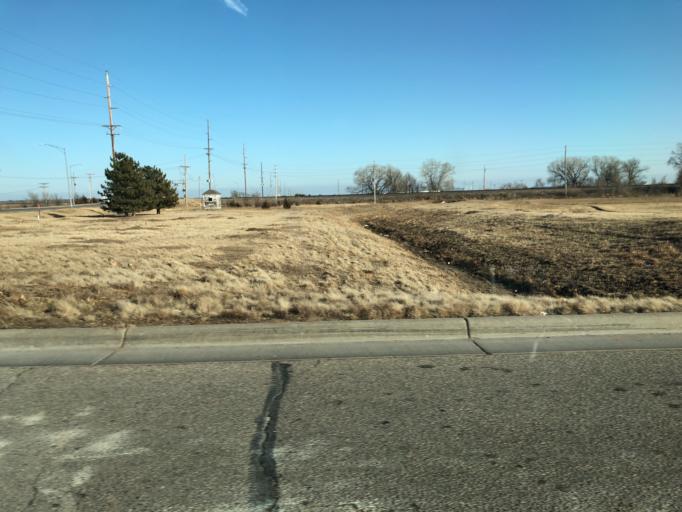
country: US
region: Kansas
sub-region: Reno County
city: Hutchinson
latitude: 38.0719
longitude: -97.8913
